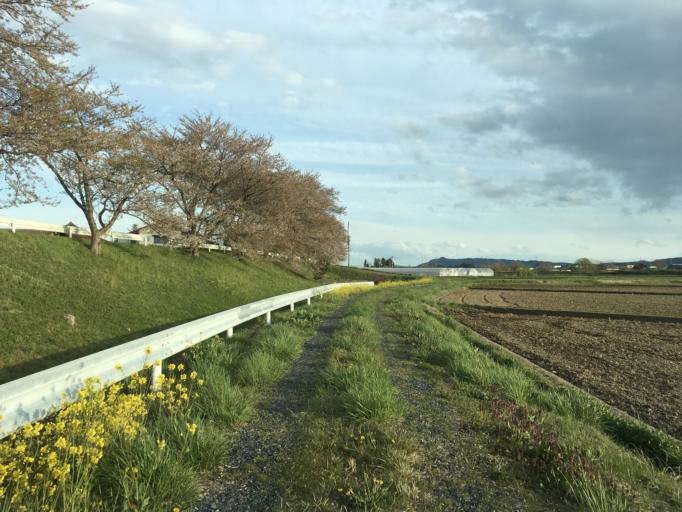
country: JP
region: Miyagi
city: Wakuya
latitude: 38.6473
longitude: 141.1453
